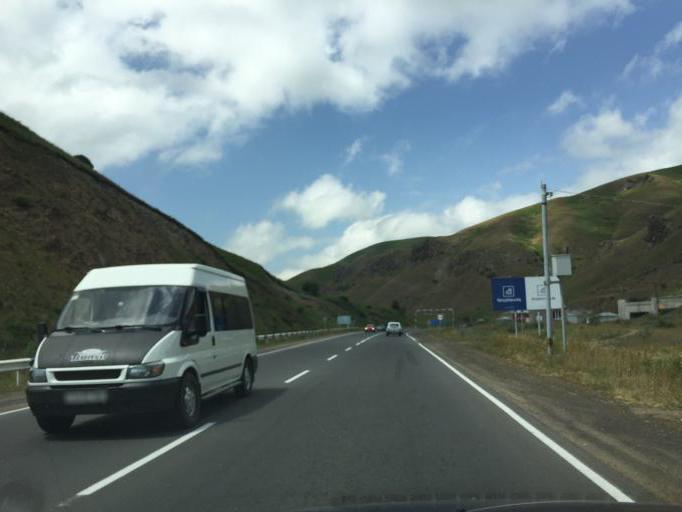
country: AM
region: Geghark'unik'i Marz
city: Tsovagyugh
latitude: 40.6523
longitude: 44.8949
